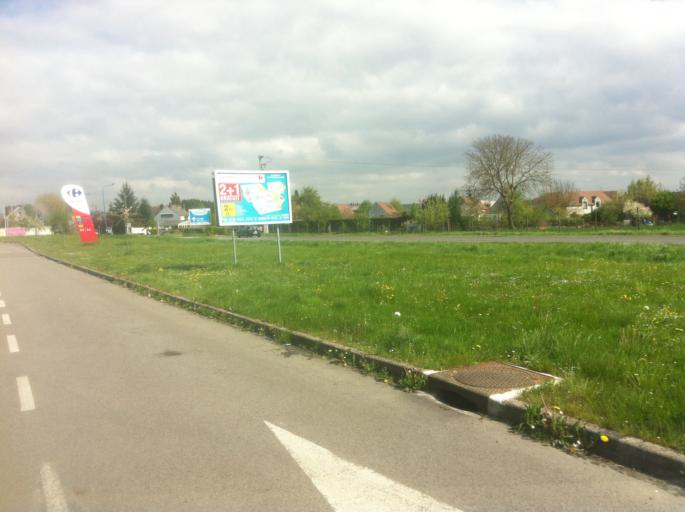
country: FR
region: Picardie
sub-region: Departement de l'Aisne
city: Villers-Cotterets
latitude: 49.2552
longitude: 3.0794
